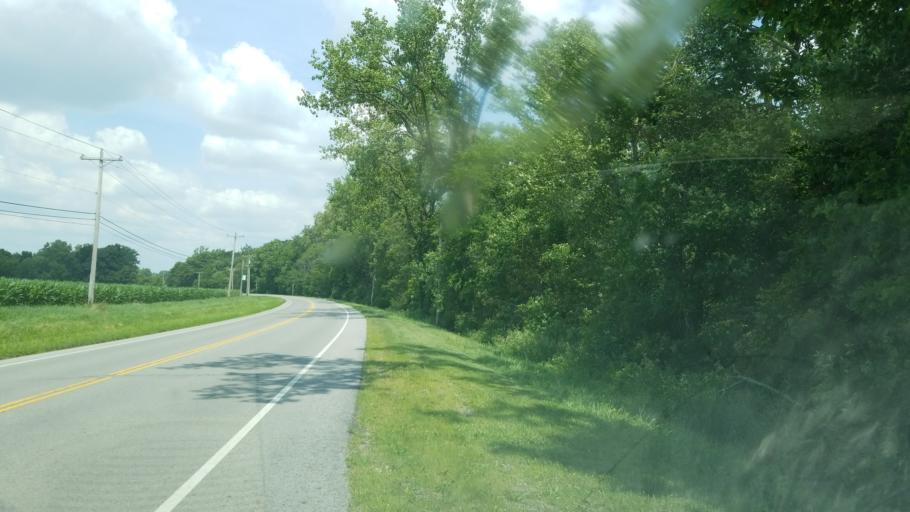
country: US
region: Ohio
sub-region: Henry County
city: Napoleon
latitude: 41.3490
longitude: -84.1456
